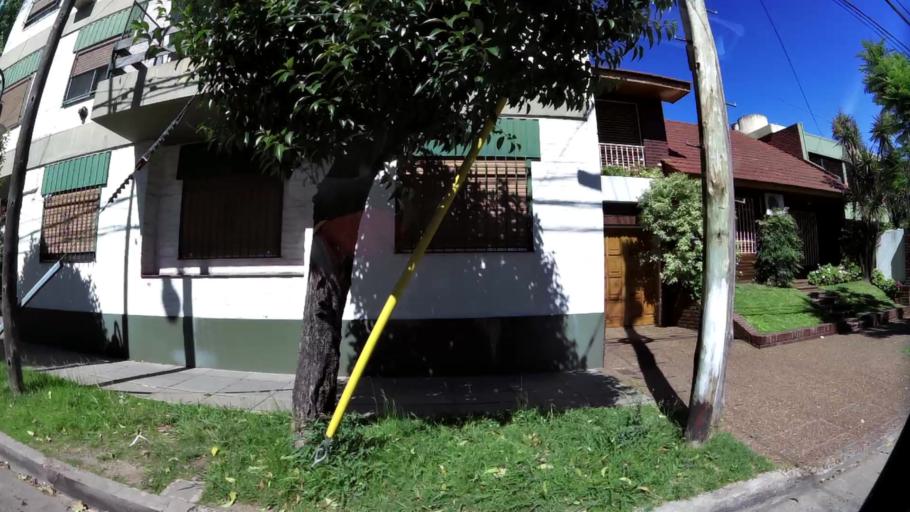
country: AR
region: Buenos Aires
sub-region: Partido de Vicente Lopez
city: Olivos
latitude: -34.5264
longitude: -58.4968
